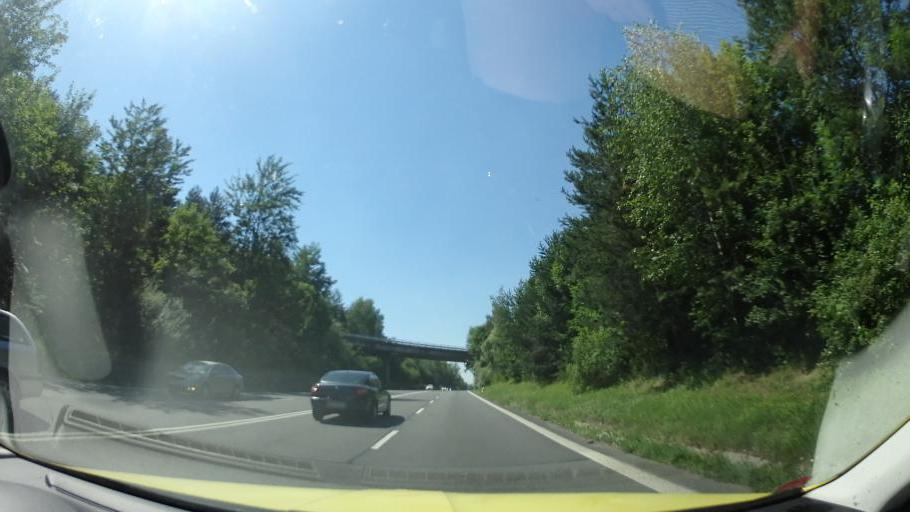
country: CZ
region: Olomoucky
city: Hustopece Nad Becvou
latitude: 49.5648
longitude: 17.8907
